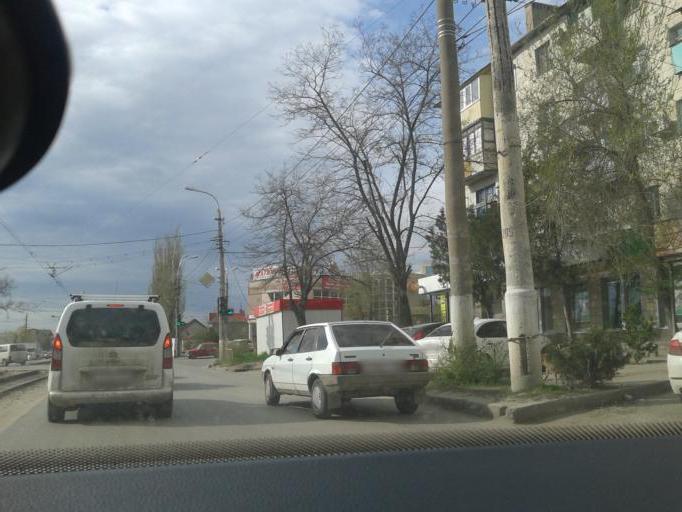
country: RU
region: Volgograd
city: Volgograd
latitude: 48.7238
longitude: 44.4683
